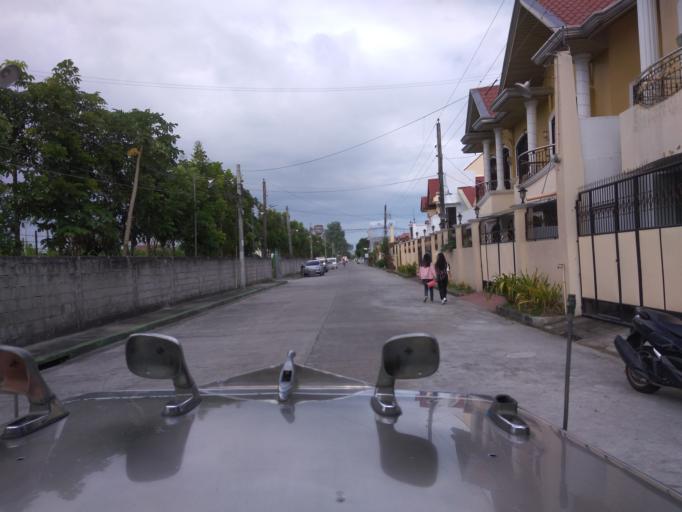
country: PH
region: Central Luzon
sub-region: Province of Pampanga
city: Pandacaqui
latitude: 15.1775
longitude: 120.6423
